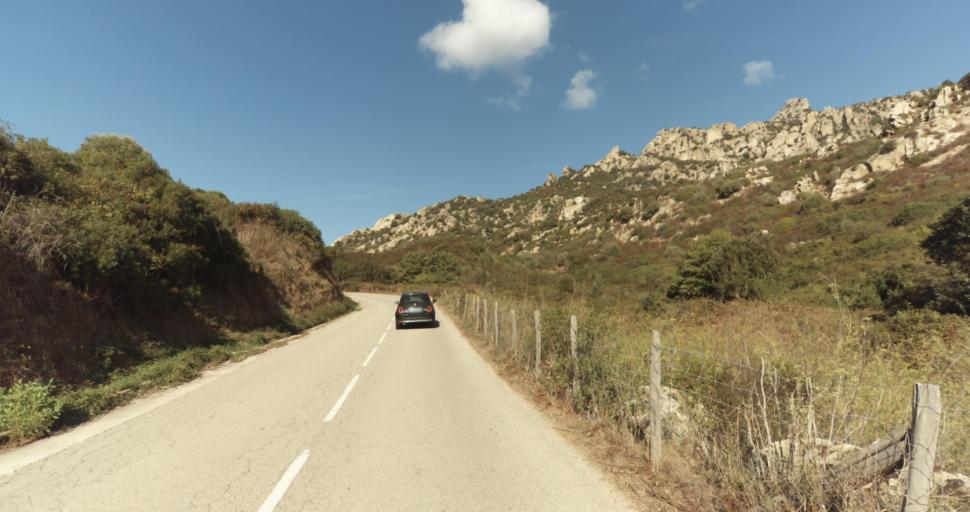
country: FR
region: Corsica
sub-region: Departement de la Corse-du-Sud
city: Ajaccio
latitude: 41.9333
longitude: 8.6871
